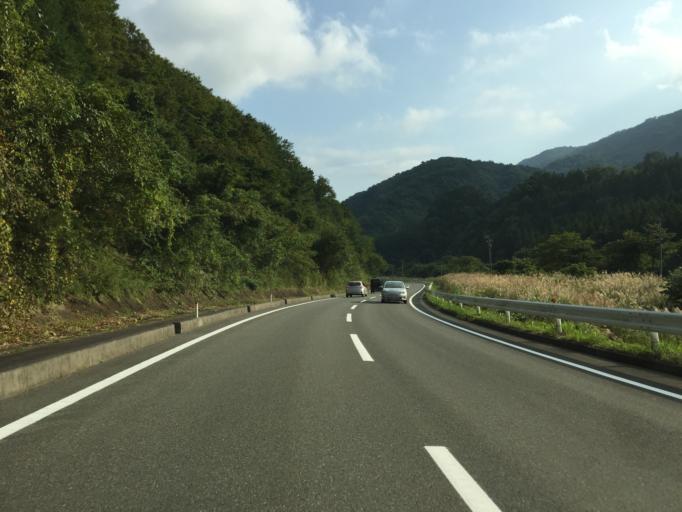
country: JP
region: Fukushima
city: Namie
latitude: 37.5463
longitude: 140.8434
